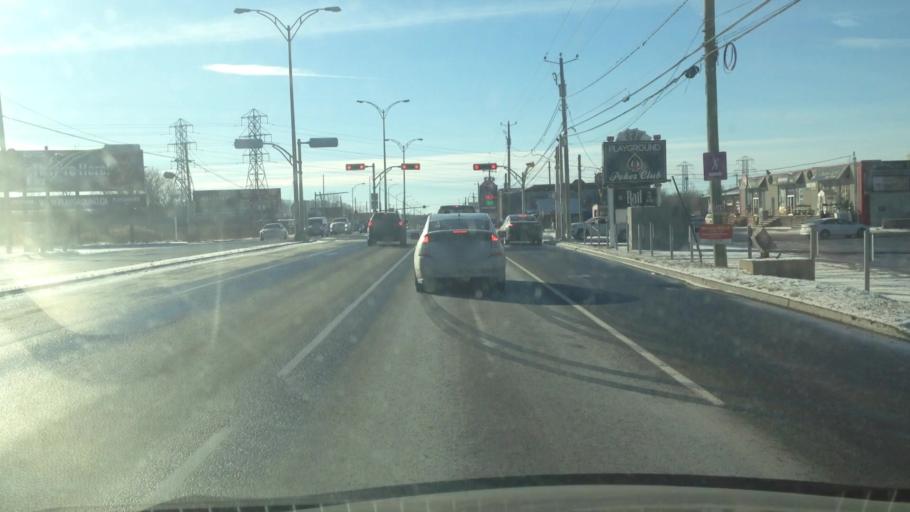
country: CA
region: Quebec
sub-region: Monteregie
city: Chateauguay
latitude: 45.3775
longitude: -73.7049
